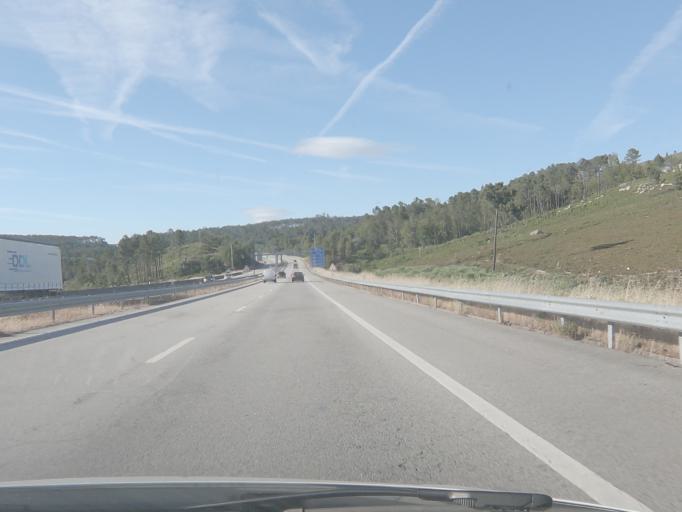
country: PT
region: Viseu
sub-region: Viseu
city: Campo
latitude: 40.7513
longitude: -7.9230
